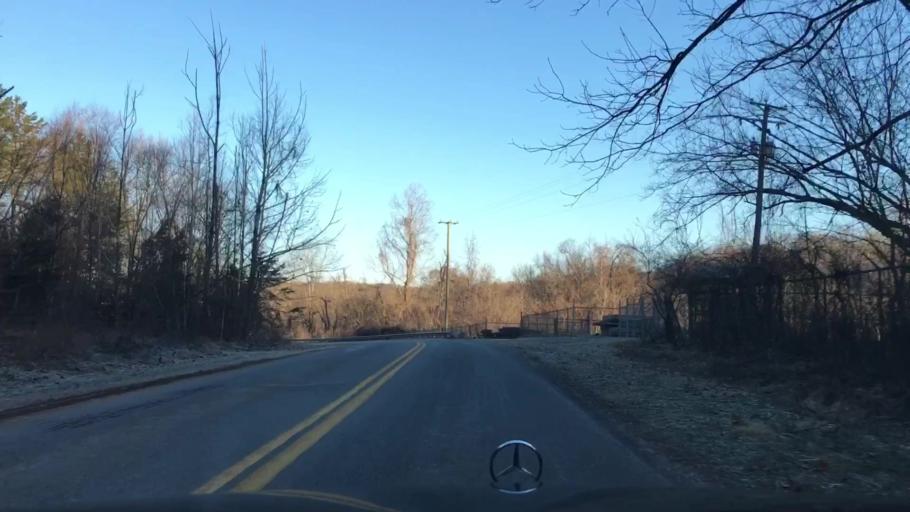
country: US
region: Virginia
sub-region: Pittsylvania County
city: Hurt
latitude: 37.1045
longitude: -79.3052
